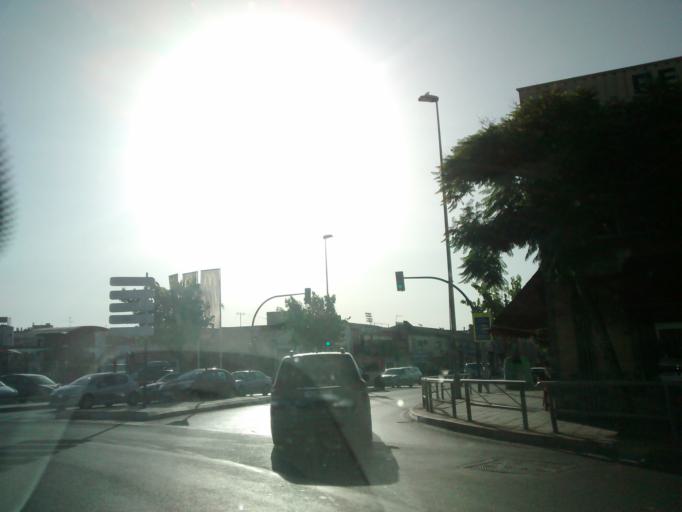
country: ES
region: Valencia
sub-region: Provincia de Alicante
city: Santa Pola
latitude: 38.1972
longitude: -0.5627
